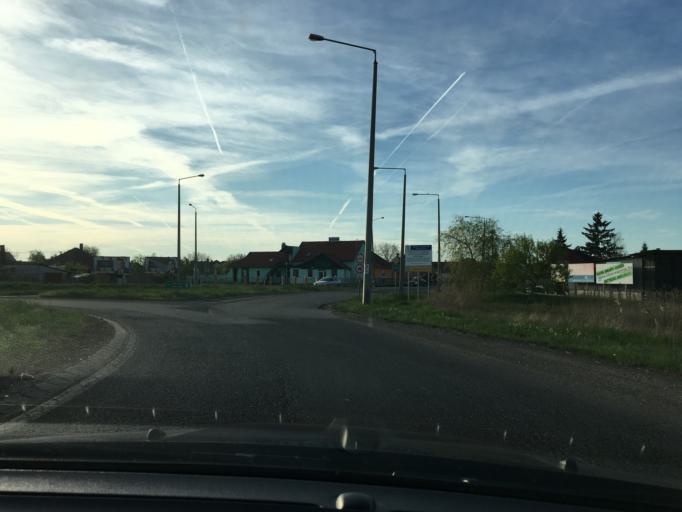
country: HU
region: Hajdu-Bihar
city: Berettyoujfalu
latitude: 47.1924
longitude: 21.5428
